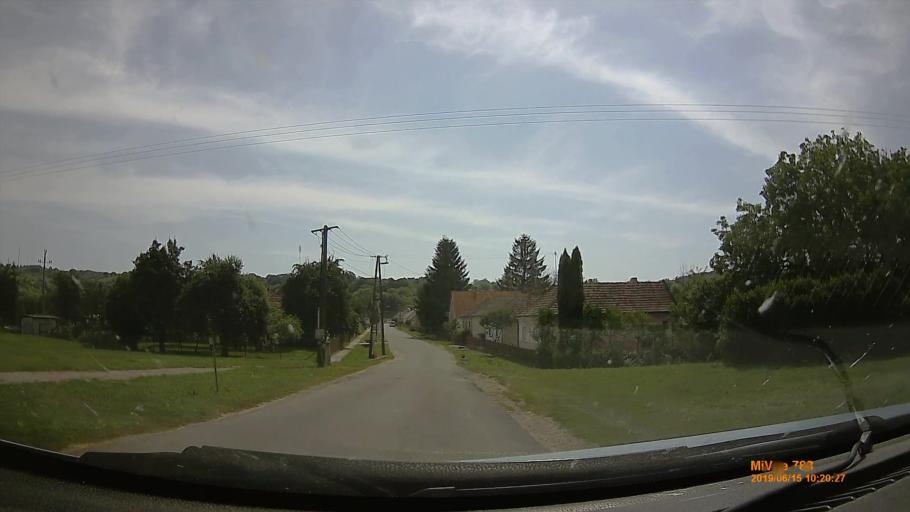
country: HU
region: Baranya
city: Buekkoesd
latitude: 46.1106
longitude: 17.9984
